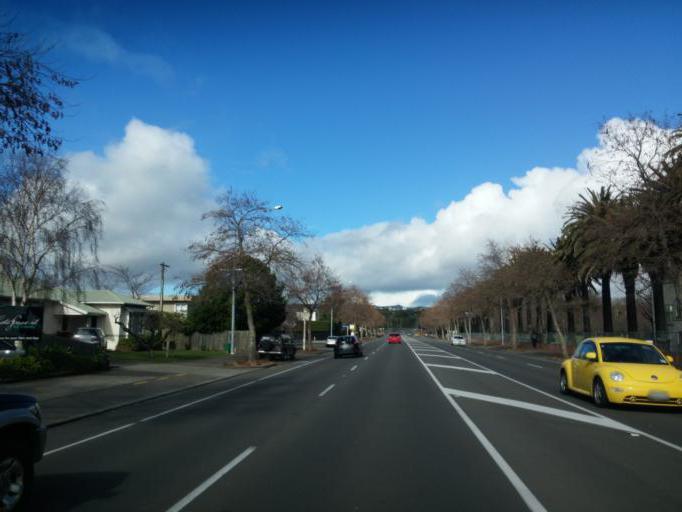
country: NZ
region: Manawatu-Wanganui
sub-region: Palmerston North City
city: Palmerston North
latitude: -40.3694
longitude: 175.6213
